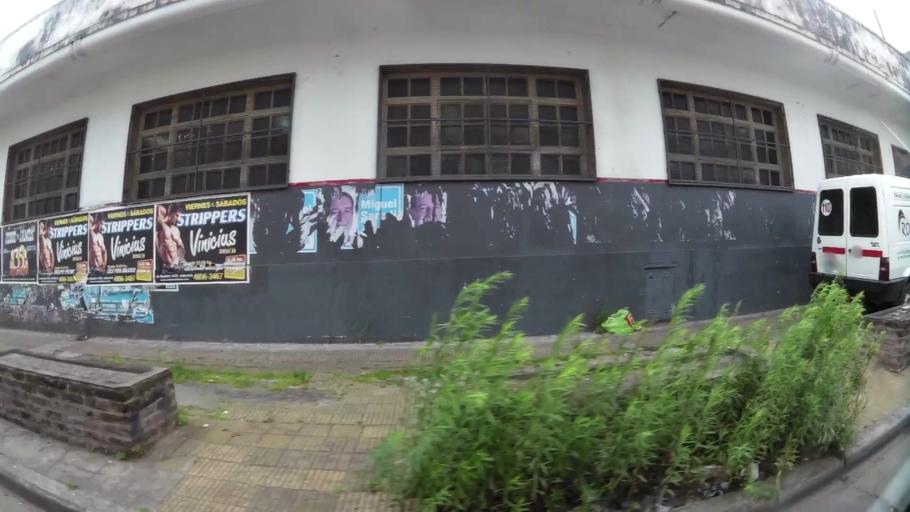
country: AR
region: Buenos Aires
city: San Justo
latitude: -34.6668
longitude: -58.5285
